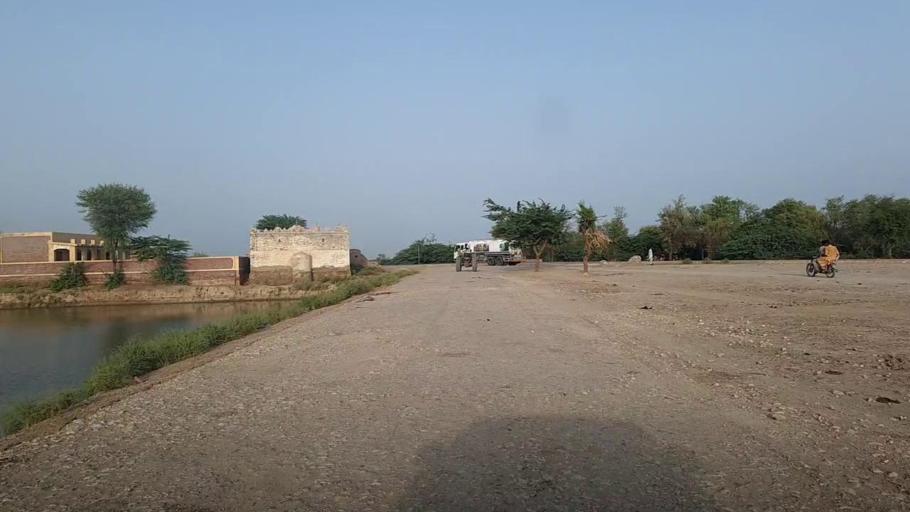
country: PK
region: Sindh
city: Mehar
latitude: 27.1632
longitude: 67.7920
